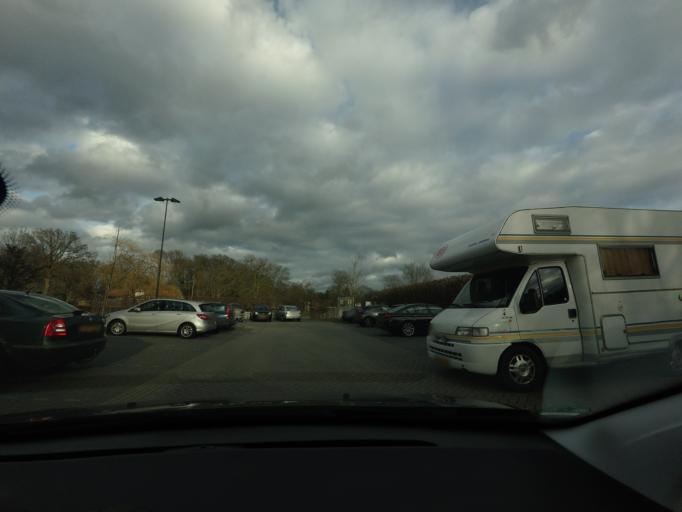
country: NL
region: Gelderland
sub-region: Gemeente Lochem
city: Gorssel
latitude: 52.1992
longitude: 6.2015
